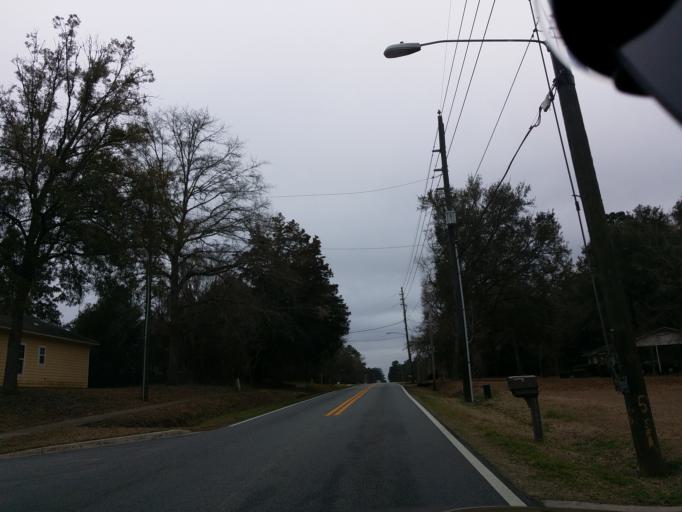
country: US
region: Florida
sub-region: Leon County
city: Tallahassee
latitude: 30.5042
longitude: -84.2300
